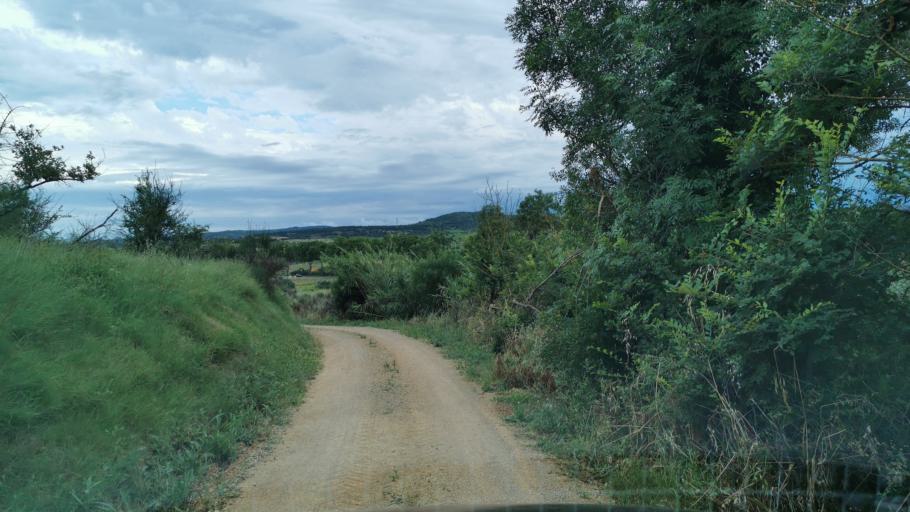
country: FR
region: Languedoc-Roussillon
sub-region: Departement de l'Aude
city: Marcorignan
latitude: 43.2220
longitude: 2.9284
